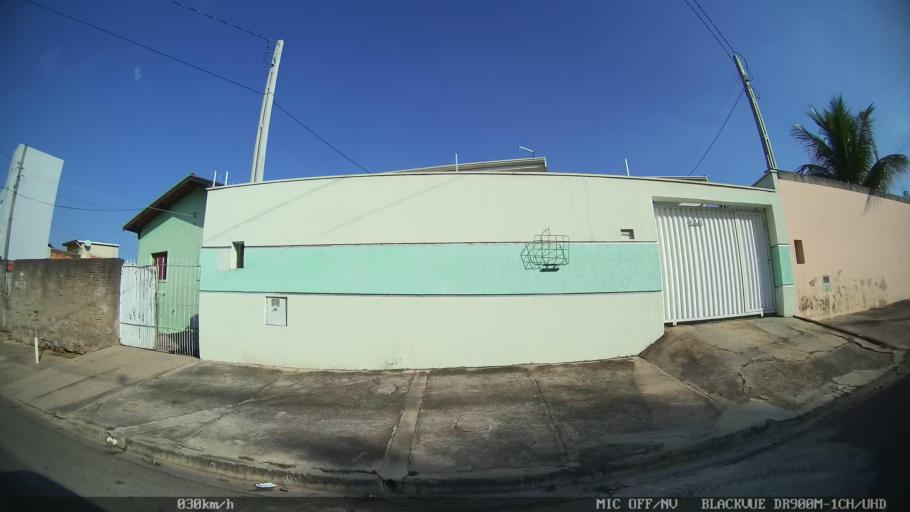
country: BR
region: Sao Paulo
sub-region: Campinas
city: Campinas
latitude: -22.9854
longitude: -47.1404
